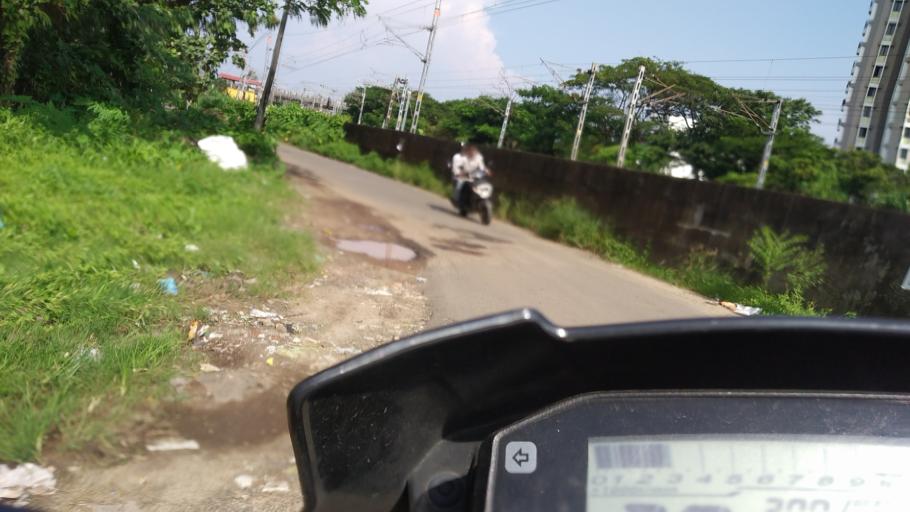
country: IN
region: Kerala
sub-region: Ernakulam
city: Cochin
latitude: 9.9803
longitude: 76.2939
